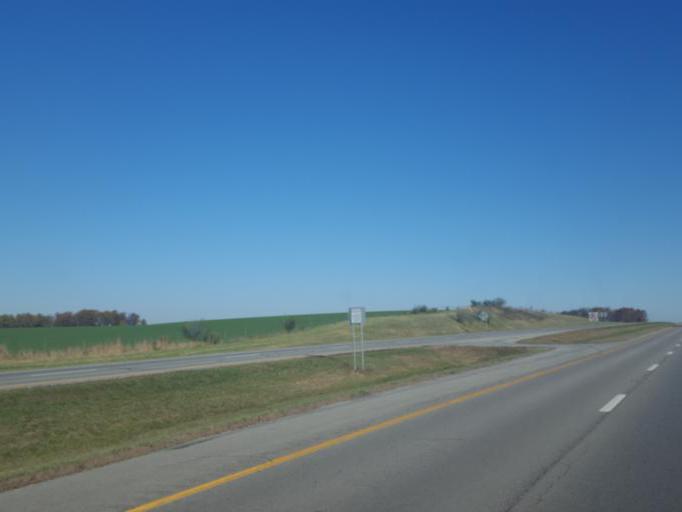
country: US
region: Ohio
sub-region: Wyandot County
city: Upper Sandusky
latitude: 40.7900
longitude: -83.2409
